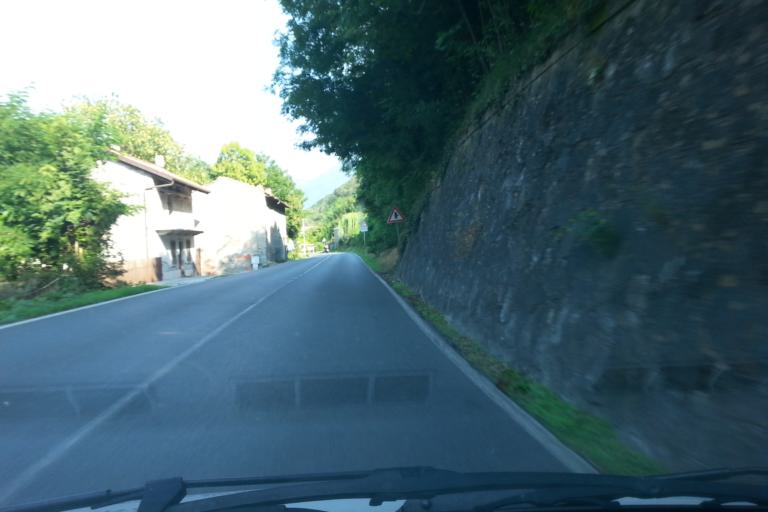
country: IT
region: Piedmont
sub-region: Provincia di Torino
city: San Didero
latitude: 45.1197
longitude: 7.2093
